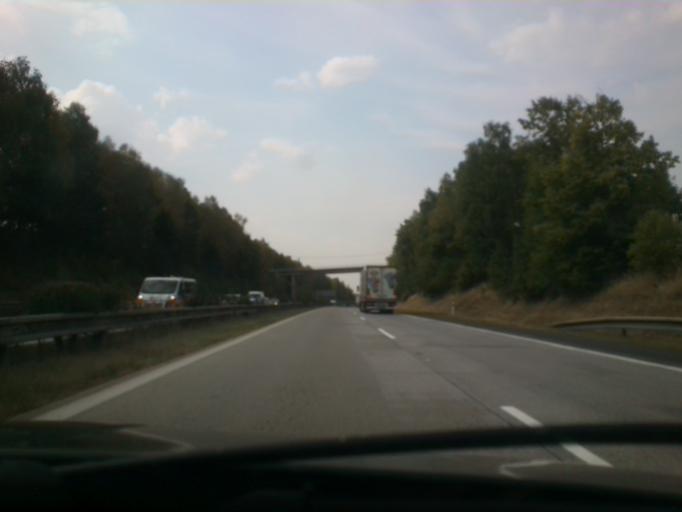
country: CZ
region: Central Bohemia
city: Ondrejov
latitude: 49.8926
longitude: 14.7488
